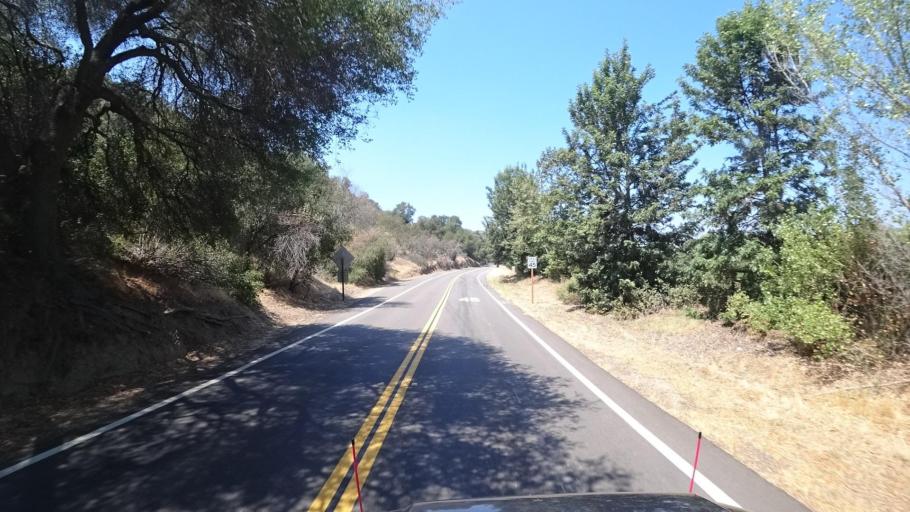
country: US
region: California
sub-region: San Diego County
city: Bonsall
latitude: 33.2721
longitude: -117.1766
